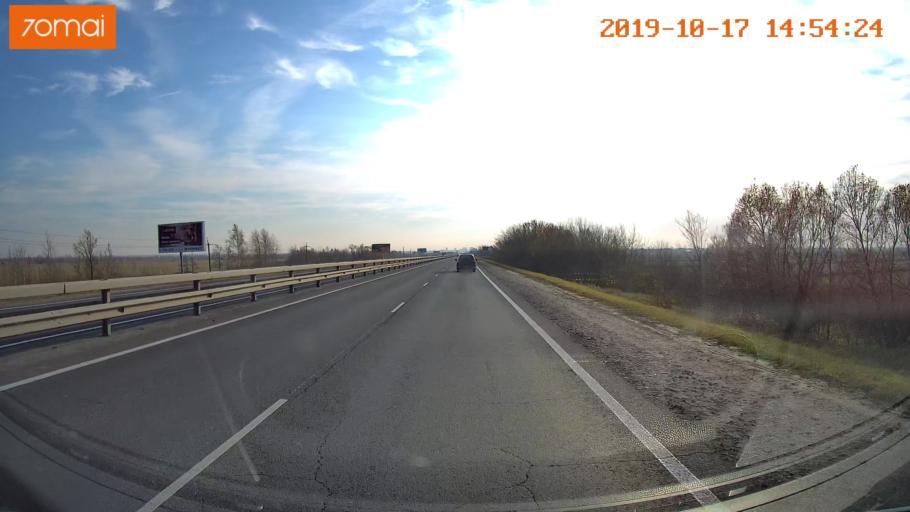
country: RU
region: Rjazan
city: Polyany
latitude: 54.6819
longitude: 39.8325
